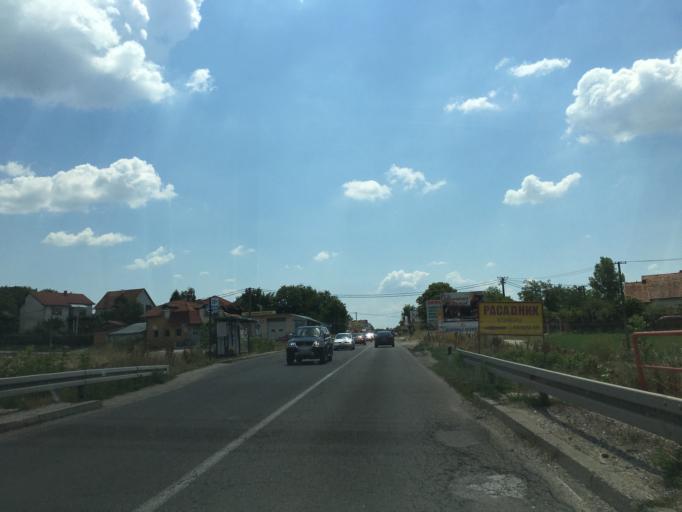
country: RS
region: Central Serbia
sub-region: Belgrade
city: Mladenovac
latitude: 44.4616
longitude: 20.6699
